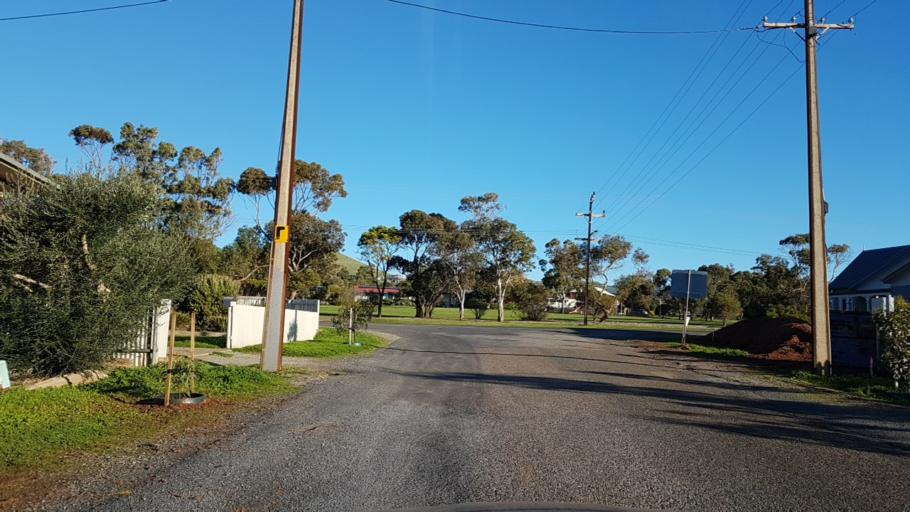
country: AU
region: South Australia
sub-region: Onkaparinga
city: Port Willunga
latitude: -35.3387
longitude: 138.4494
